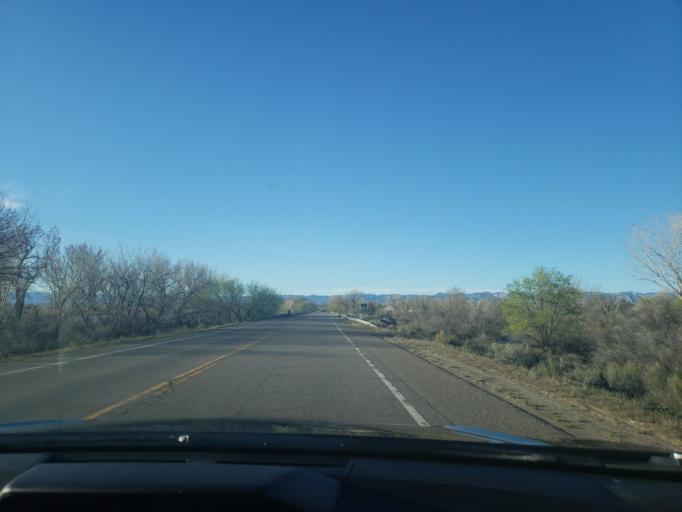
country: US
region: Colorado
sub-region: Mesa County
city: Fruita
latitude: 39.1399
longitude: -108.7383
